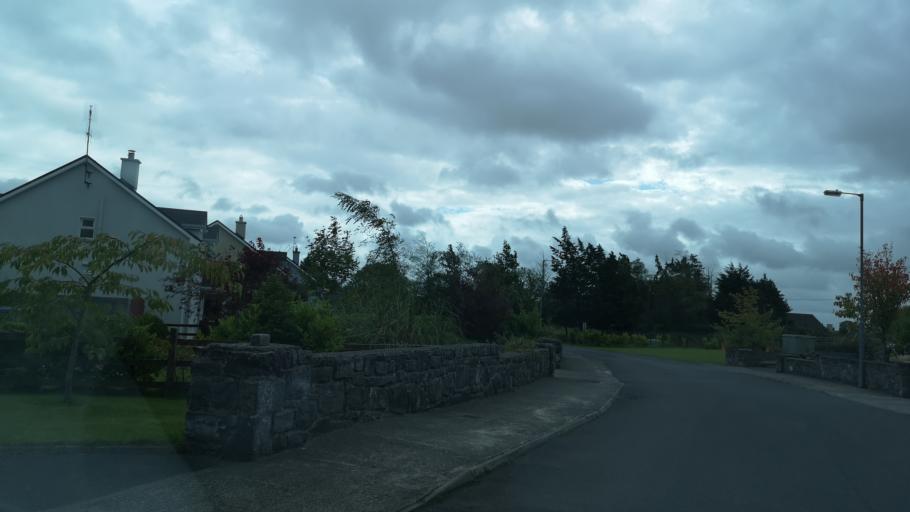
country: IE
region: Connaught
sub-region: County Galway
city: Athenry
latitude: 53.2764
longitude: -8.6399
